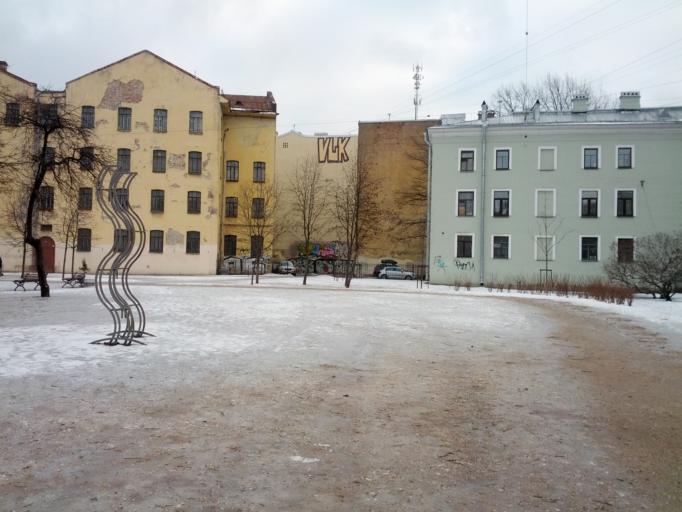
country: RU
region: St.-Petersburg
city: Petrogradka
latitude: 59.9570
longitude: 30.3015
